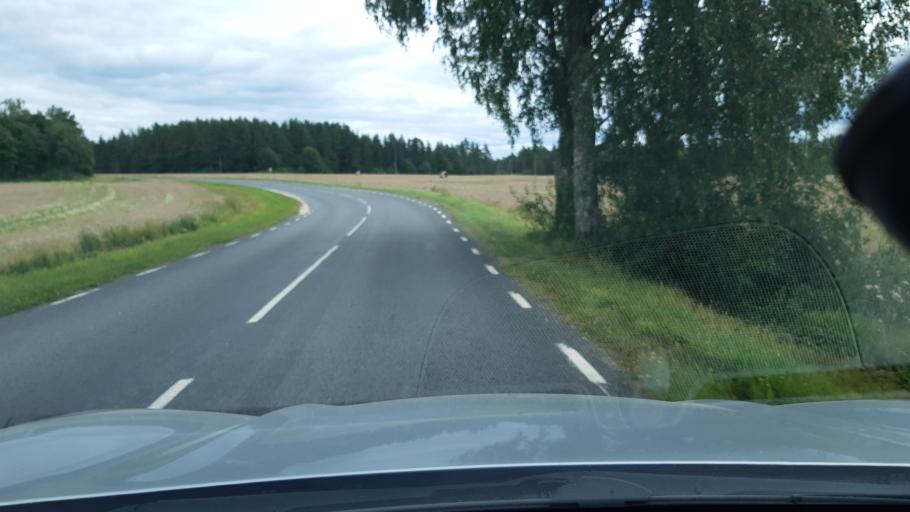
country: EE
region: Raplamaa
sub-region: Maerjamaa vald
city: Marjamaa
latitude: 59.0394
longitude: 24.4944
